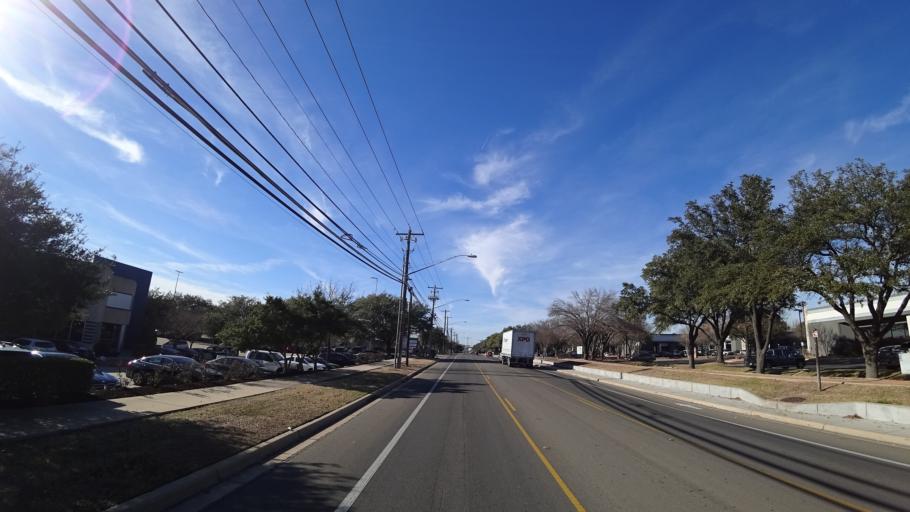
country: US
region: Texas
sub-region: Travis County
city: Wells Branch
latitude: 30.3876
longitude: -97.7081
